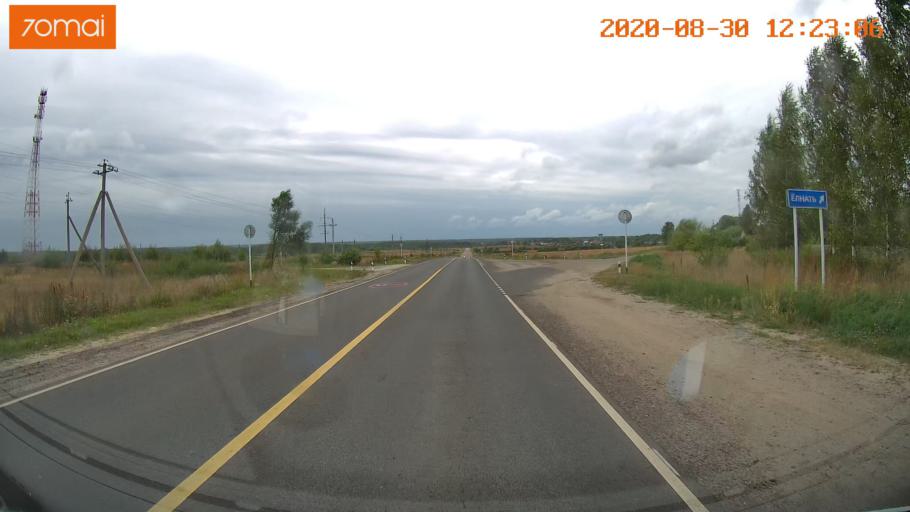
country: RU
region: Ivanovo
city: Yur'yevets
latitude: 57.3310
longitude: 42.8325
